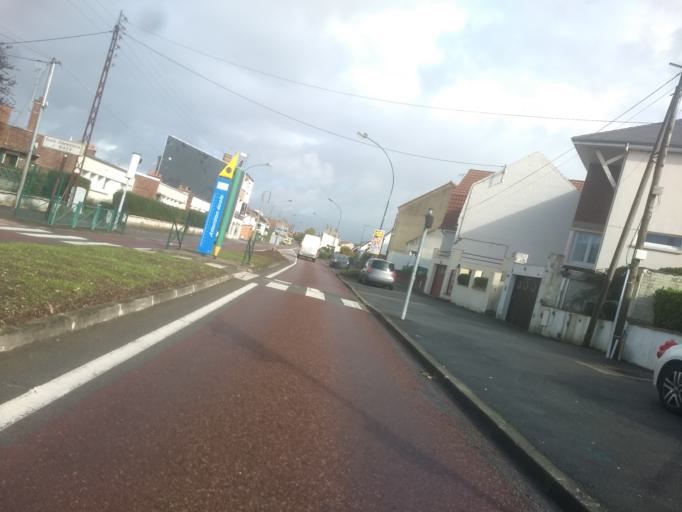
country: FR
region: Nord-Pas-de-Calais
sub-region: Departement du Pas-de-Calais
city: Achicourt
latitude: 50.2719
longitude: 2.7746
